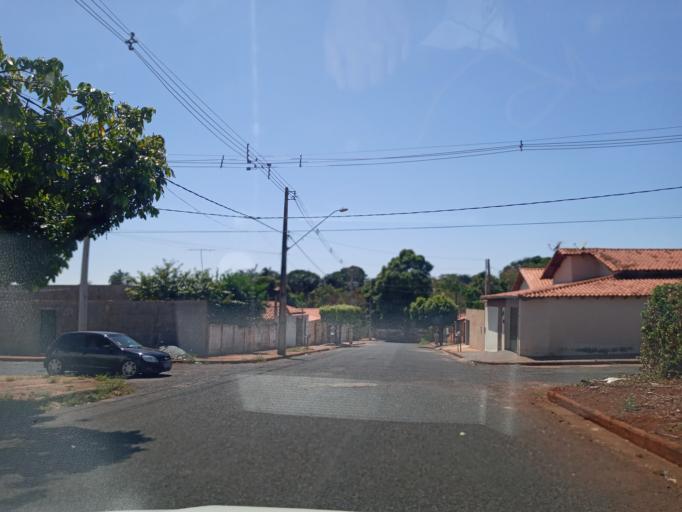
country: BR
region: Minas Gerais
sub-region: Ituiutaba
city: Ituiutaba
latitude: -18.9588
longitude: -49.4535
